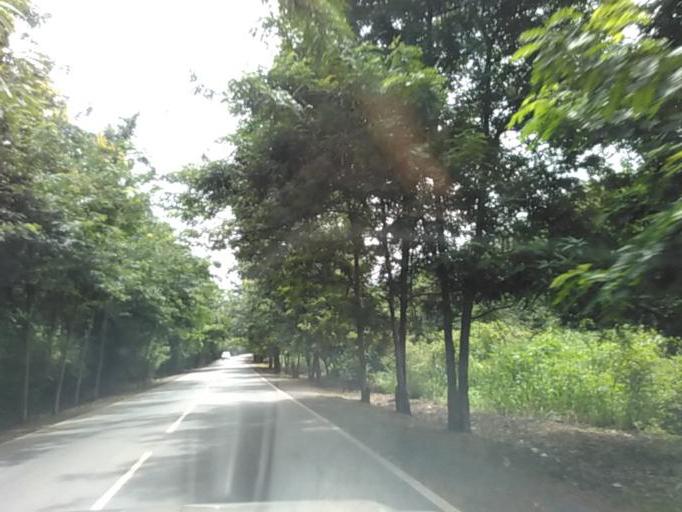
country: GH
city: Akropong
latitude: 6.2643
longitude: 0.0634
